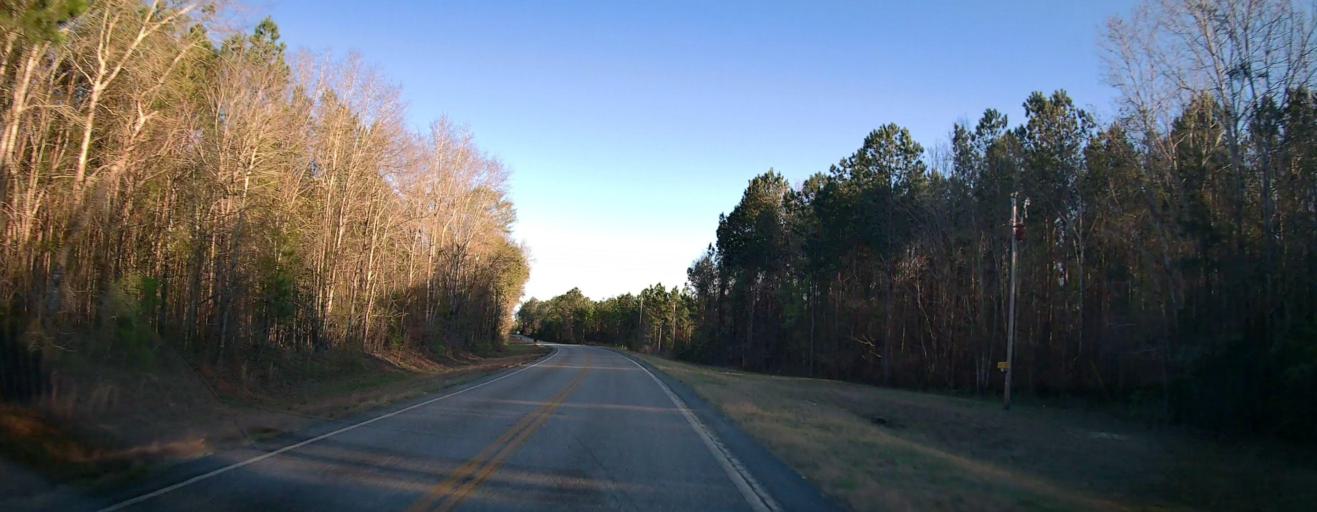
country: US
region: Georgia
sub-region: Wilcox County
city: Abbeville
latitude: 32.0711
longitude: -83.2829
